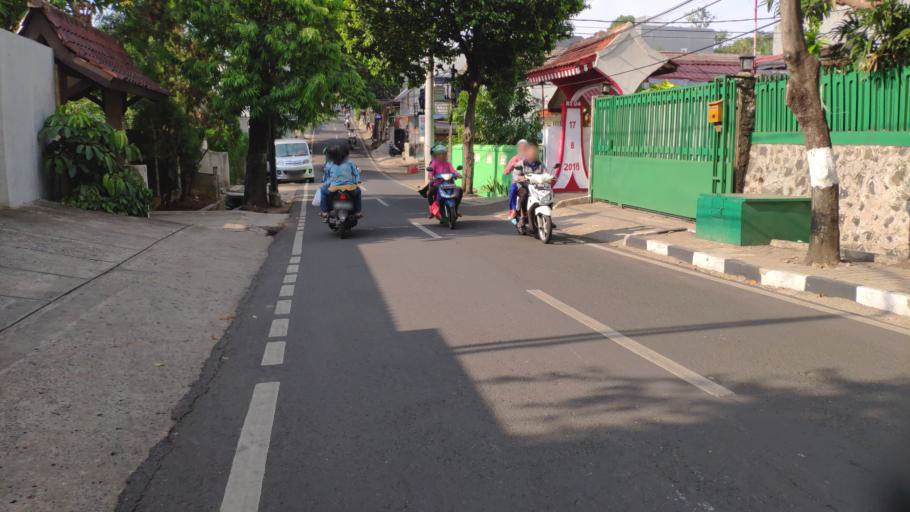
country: ID
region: West Java
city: Pamulang
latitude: -6.3062
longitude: 106.7986
